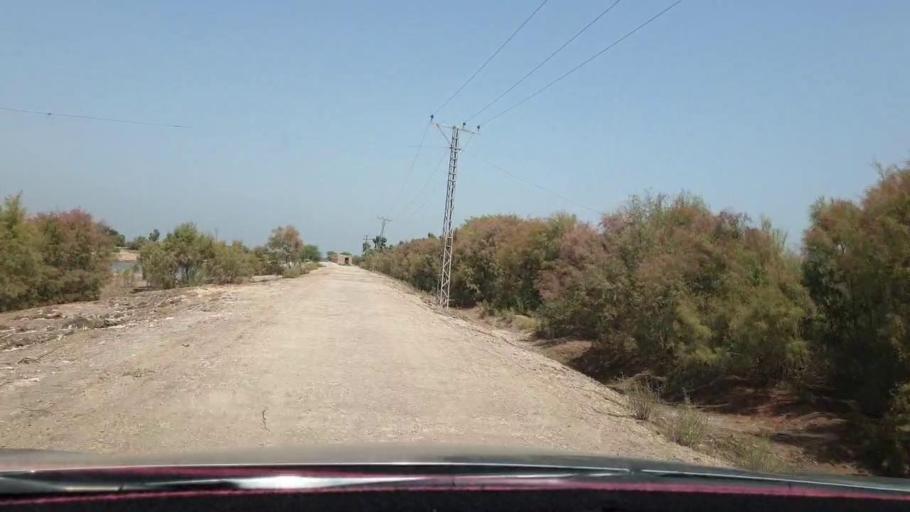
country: PK
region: Sindh
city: Warah
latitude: 27.4086
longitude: 67.6969
